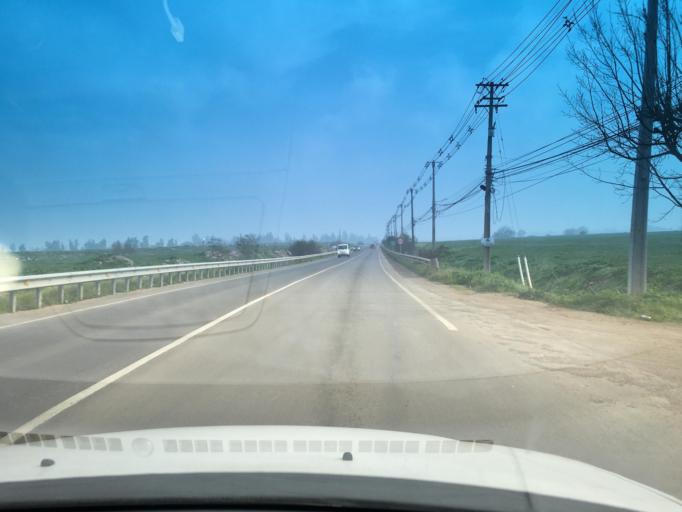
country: CL
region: Santiago Metropolitan
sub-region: Provincia de Chacabuco
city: Lampa
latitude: -33.3498
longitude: -70.8045
